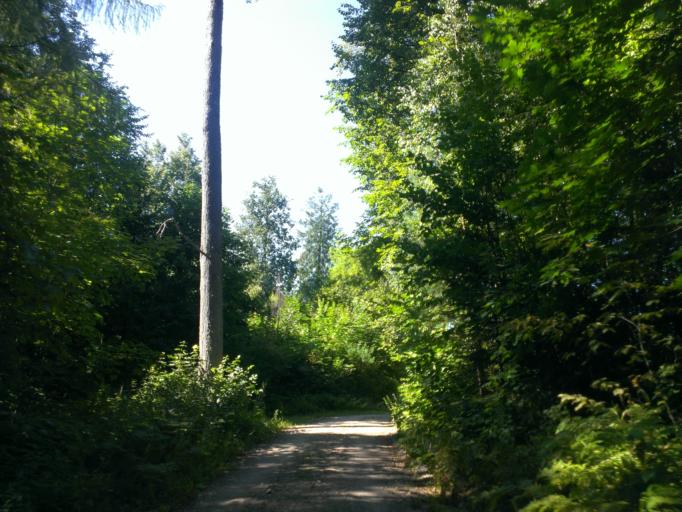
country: LV
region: Sigulda
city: Sigulda
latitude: 57.1074
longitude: 24.8132
